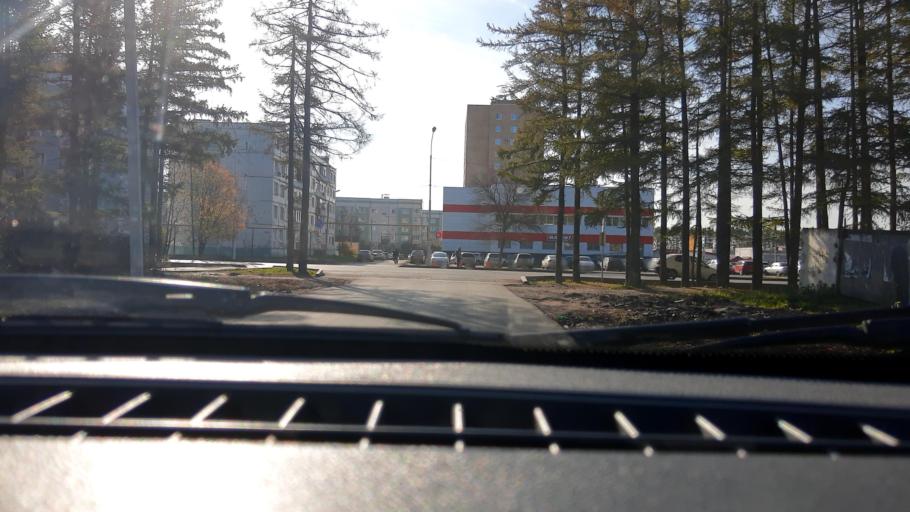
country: RU
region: Bashkortostan
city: Mikhaylovka
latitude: 54.7936
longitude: 55.8610
